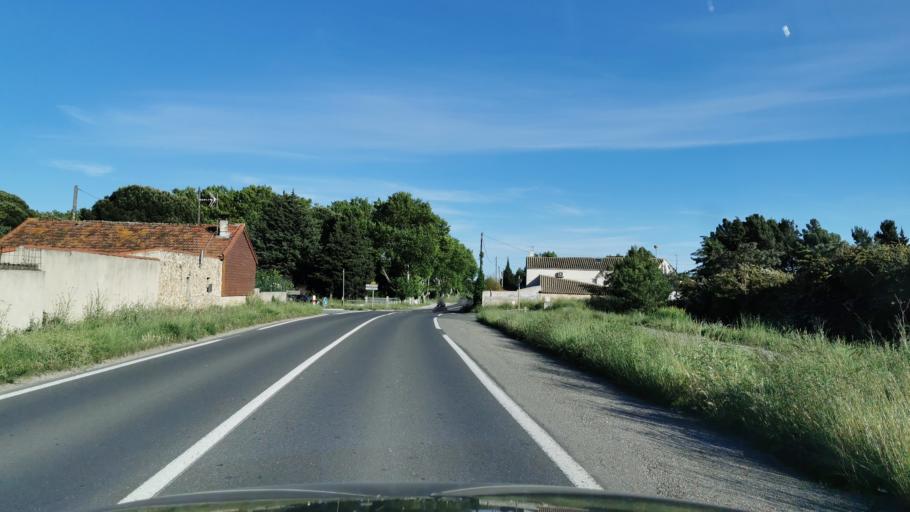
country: FR
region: Languedoc-Roussillon
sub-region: Departement de l'Aude
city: Narbonne
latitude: 43.1967
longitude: 2.9767
